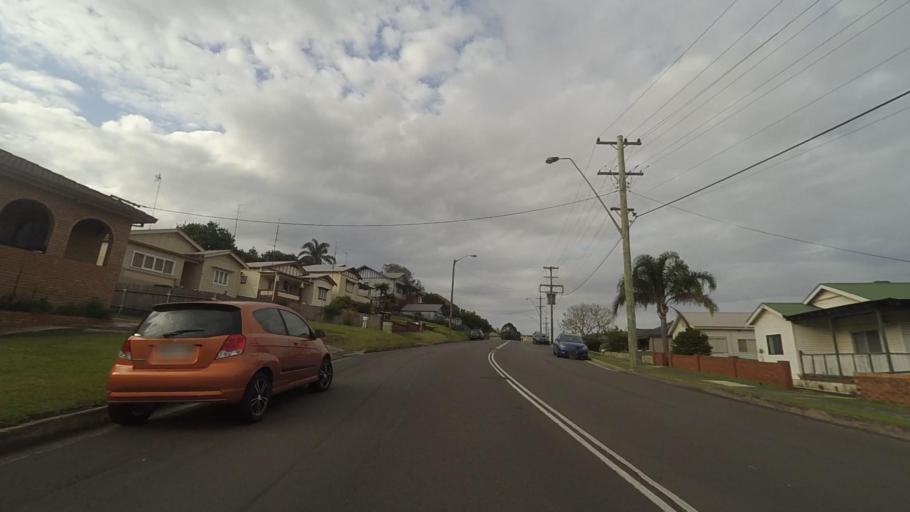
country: AU
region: New South Wales
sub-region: Wollongong
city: Wollongong
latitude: -34.4322
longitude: 150.8861
